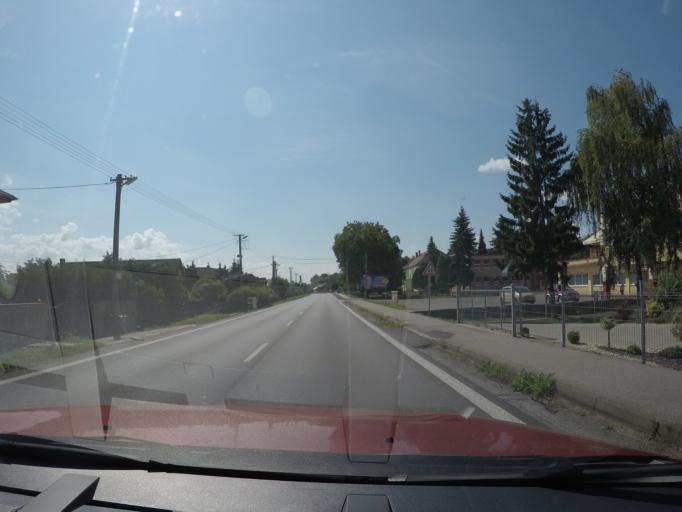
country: SK
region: Presovsky
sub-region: Okres Presov
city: Presov
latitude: 48.8748
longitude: 21.2474
